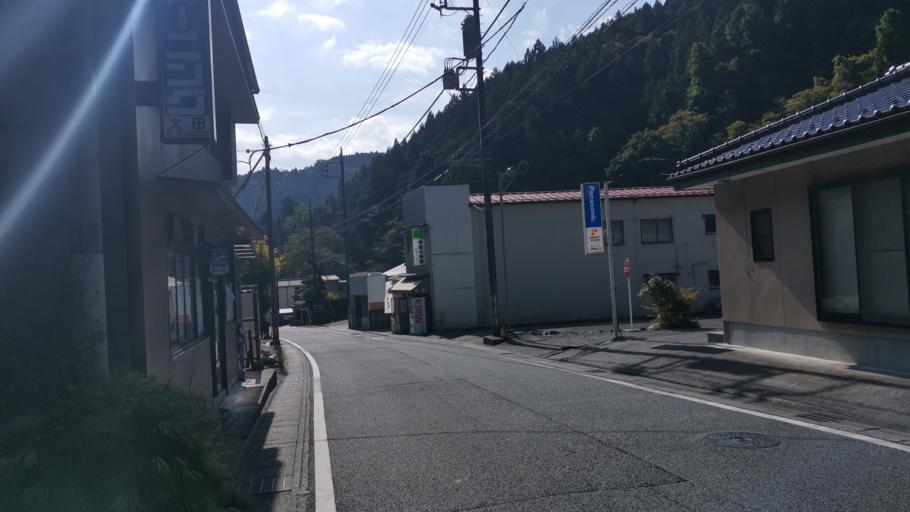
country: JP
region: Shizuoka
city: Fujinomiya
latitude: 35.3719
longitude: 138.4251
